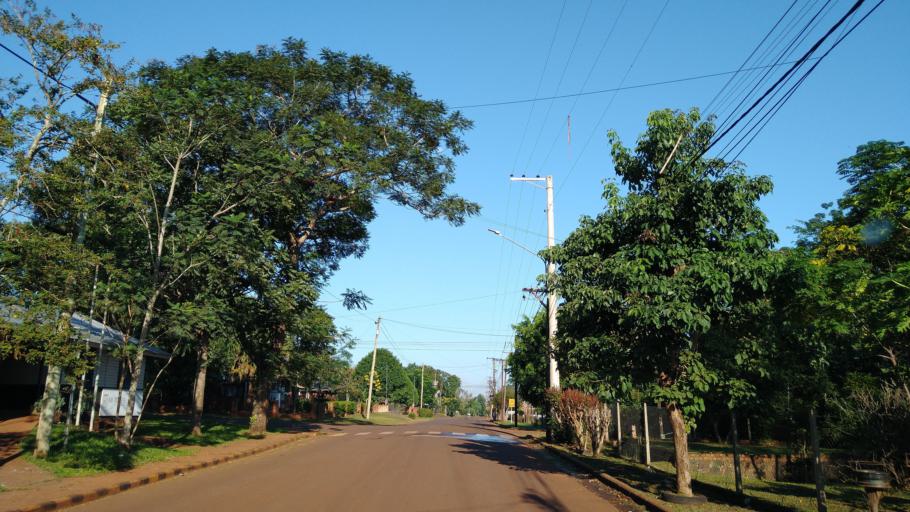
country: AR
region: Misiones
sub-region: Departamento de Montecarlo
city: Montecarlo
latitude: -26.5651
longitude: -54.7564
